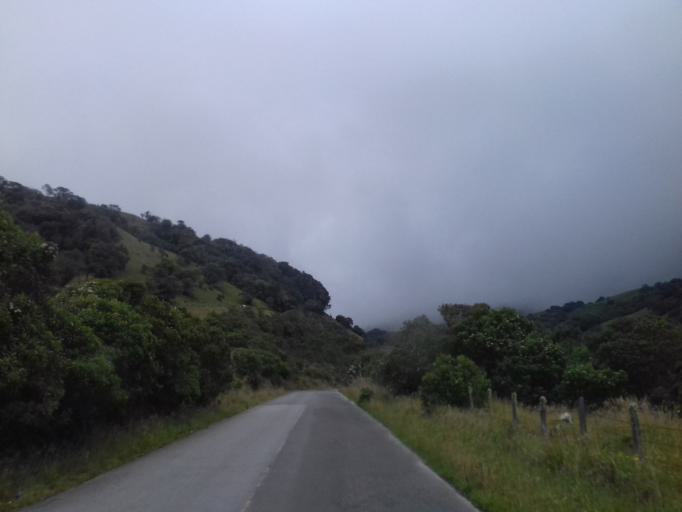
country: CO
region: Tolima
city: Herveo
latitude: 5.0142
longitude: -75.3288
